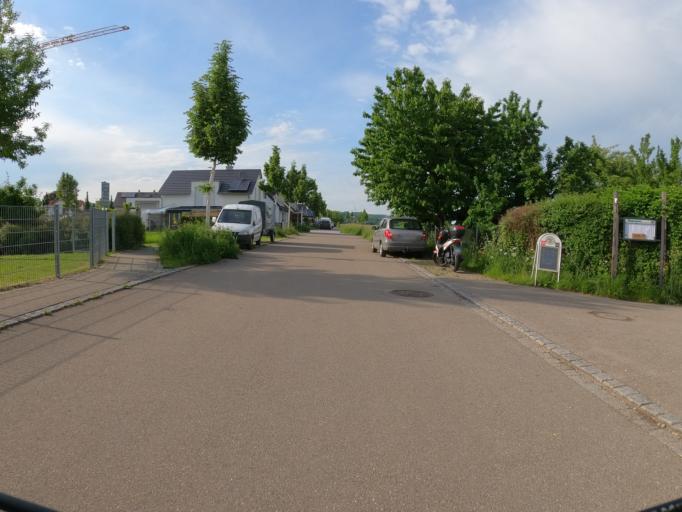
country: DE
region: Bavaria
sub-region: Swabia
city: Neu-Ulm
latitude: 48.4129
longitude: 10.0425
